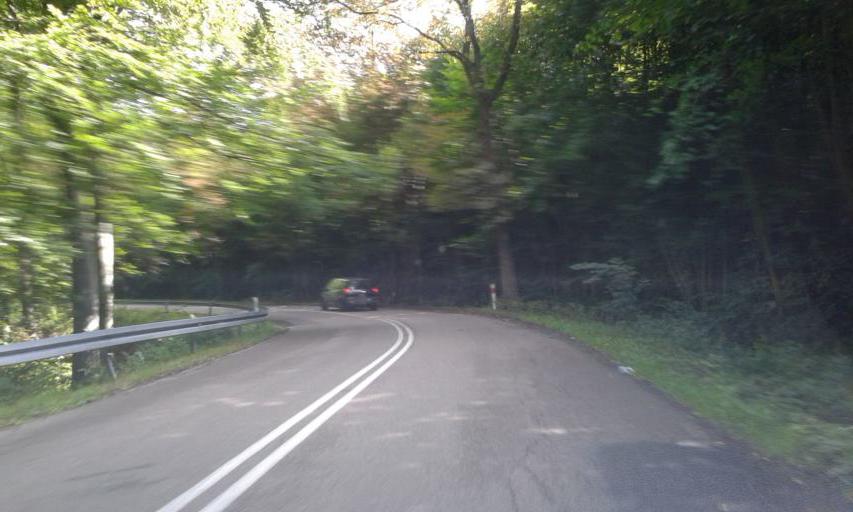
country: PL
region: West Pomeranian Voivodeship
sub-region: Powiat koszalinski
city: Polanow
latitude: 54.0000
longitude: 16.7155
